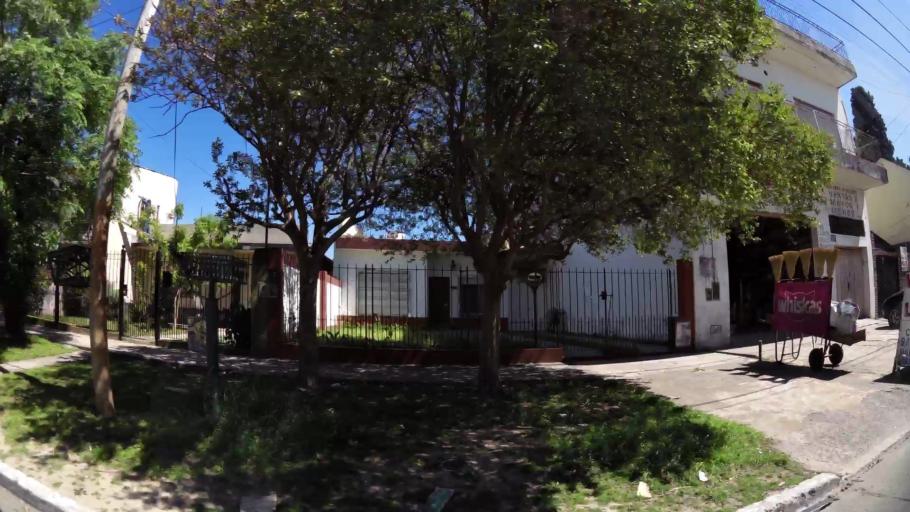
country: AR
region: Buenos Aires
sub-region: Partido de Quilmes
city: Quilmes
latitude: -34.7184
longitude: -58.3073
